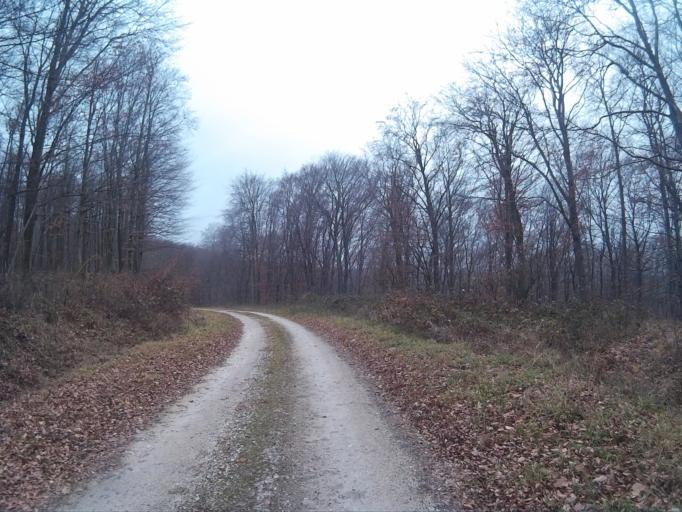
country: HU
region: Veszprem
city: Tapolca
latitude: 46.9748
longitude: 17.5068
